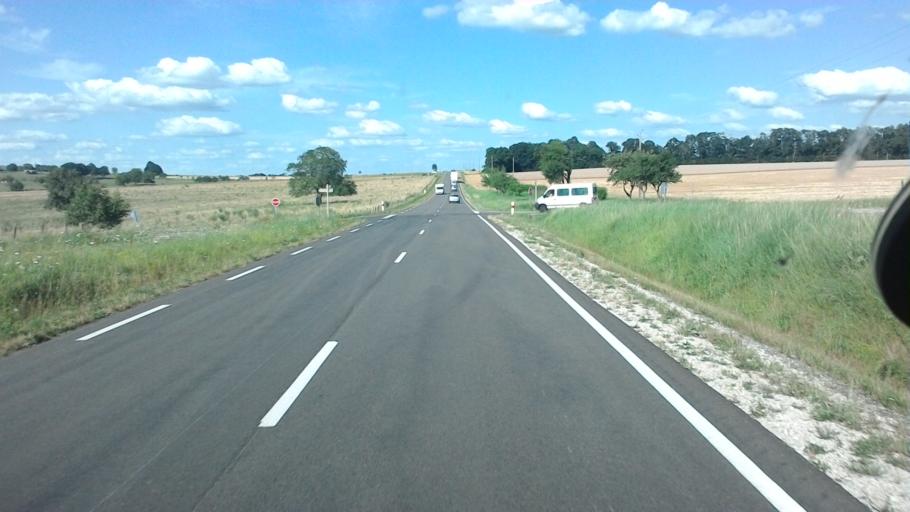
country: FR
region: Franche-Comte
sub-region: Departement de la Haute-Saone
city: Gy
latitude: 47.4567
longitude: 5.9029
